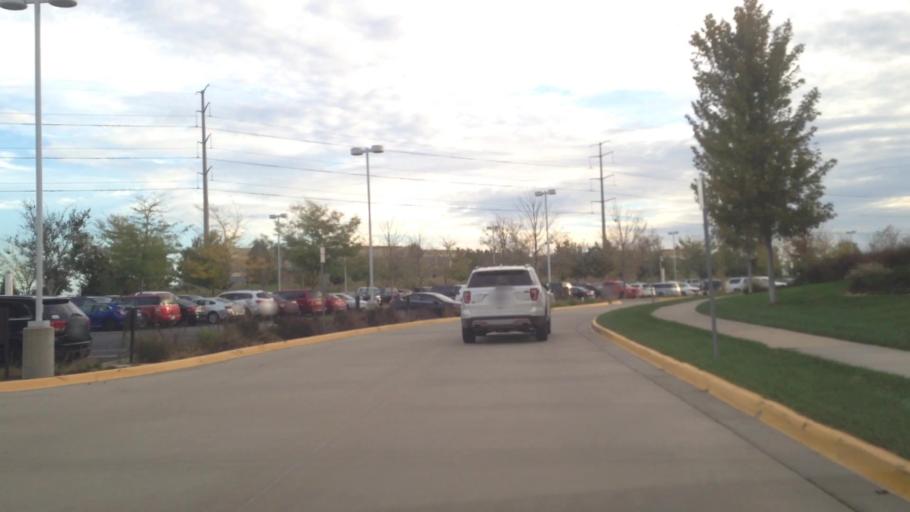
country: US
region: Kansas
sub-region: Johnson County
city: Olathe
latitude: 38.9334
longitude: -94.7964
